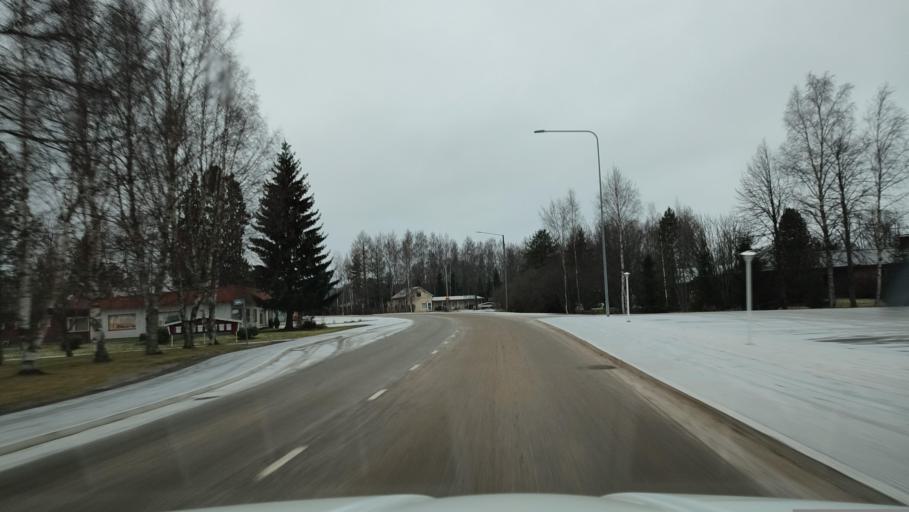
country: FI
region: Southern Ostrobothnia
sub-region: Suupohja
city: Karijoki
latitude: 62.3077
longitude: 21.7057
